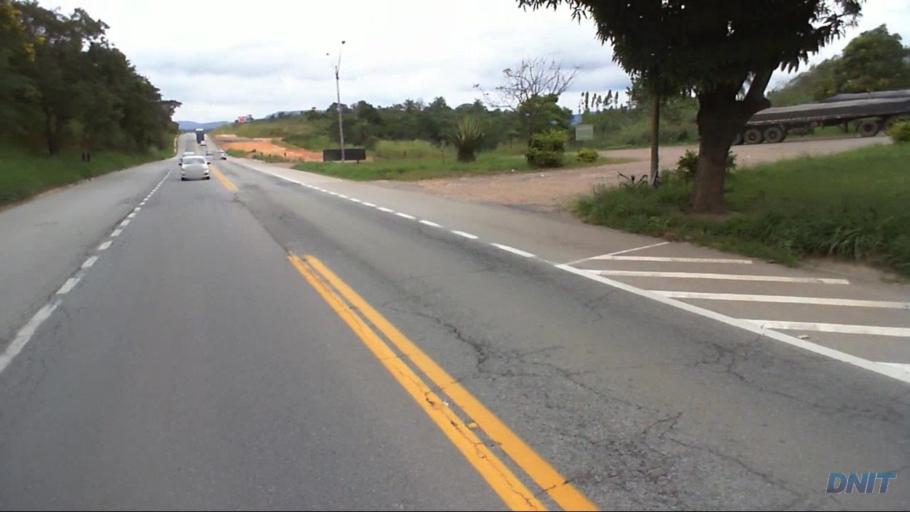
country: BR
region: Minas Gerais
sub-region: Barao De Cocais
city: Barao de Cocais
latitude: -19.7730
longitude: -43.4459
